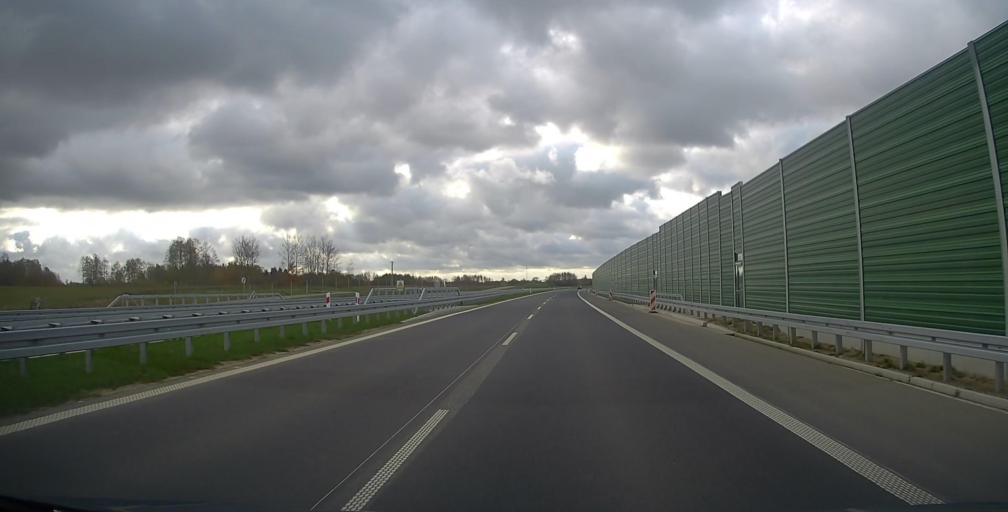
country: PL
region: Podlasie
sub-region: Powiat suwalski
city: Raczki
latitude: 53.9227
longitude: 22.7478
